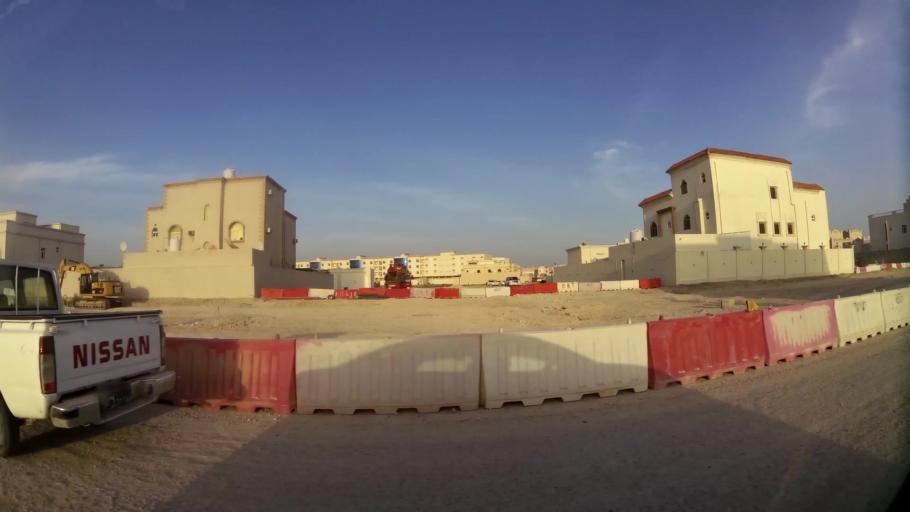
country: QA
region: Al Wakrah
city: Al Wakrah
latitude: 25.1487
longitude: 51.5949
